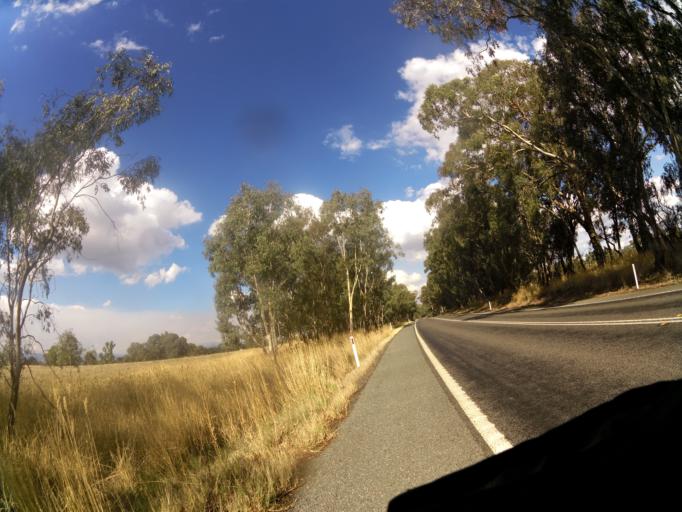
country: AU
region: Victoria
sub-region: Mansfield
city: Mansfield
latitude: -36.9869
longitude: 146.0359
